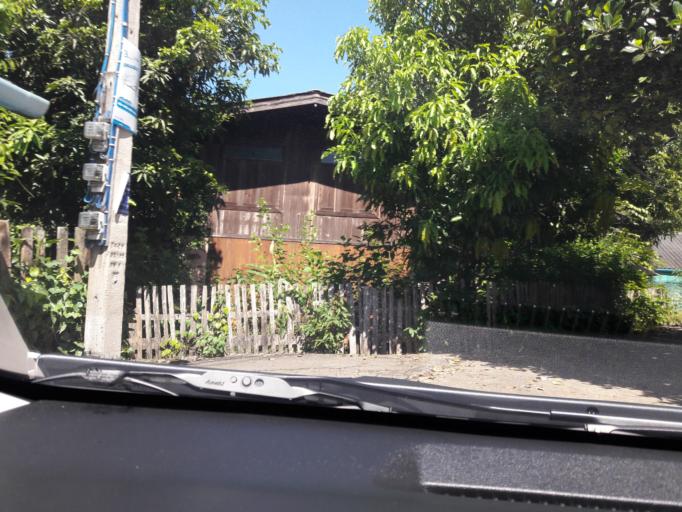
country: TH
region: Mae Hong Son
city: Mae Hong Son
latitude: 19.4229
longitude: 97.9976
